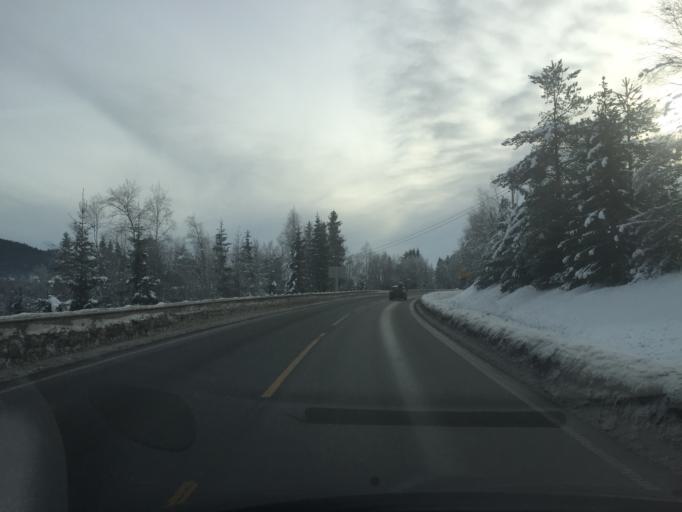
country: NO
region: Hedmark
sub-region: Trysil
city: Innbygda
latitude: 61.2697
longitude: 12.3031
